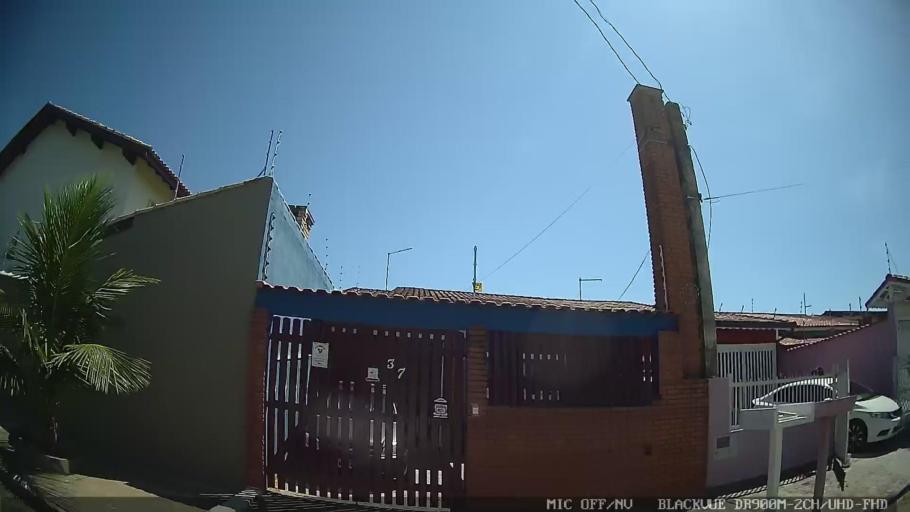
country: BR
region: Sao Paulo
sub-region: Peruibe
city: Peruibe
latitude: -24.3021
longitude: -46.9821
